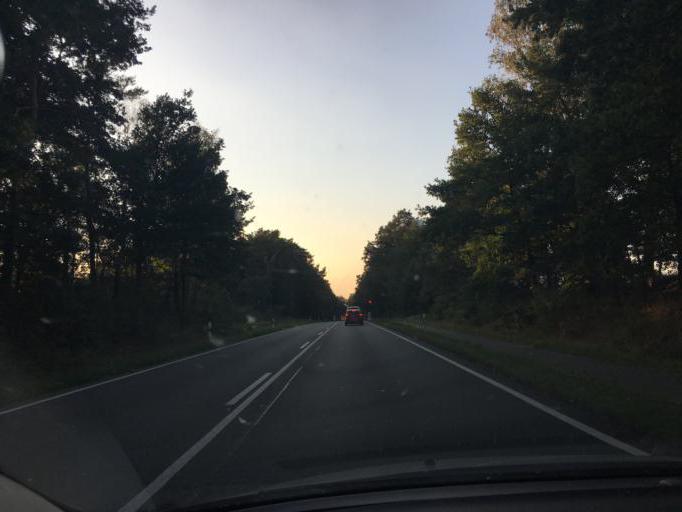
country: DE
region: Lower Saxony
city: Soltau
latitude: 52.9373
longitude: 9.8916
